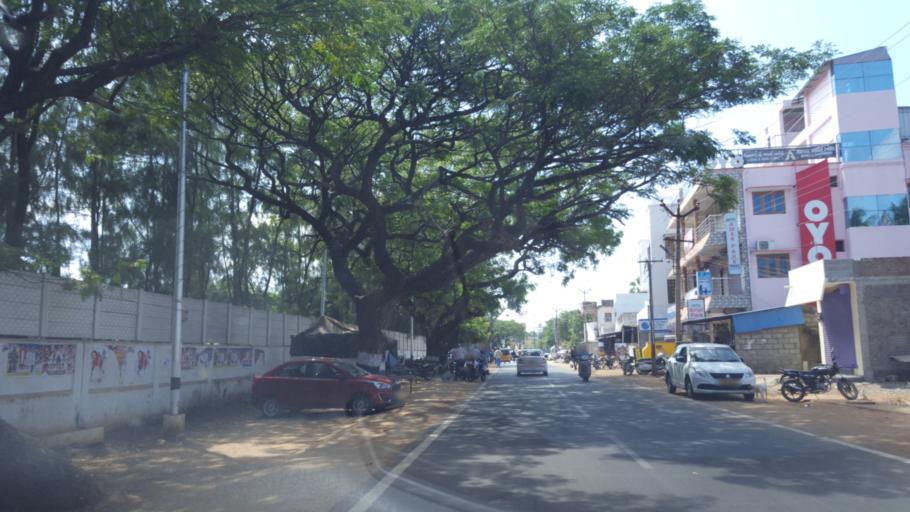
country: IN
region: Tamil Nadu
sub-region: Kancheepuram
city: Mamallapuram
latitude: 12.6245
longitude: 80.1942
